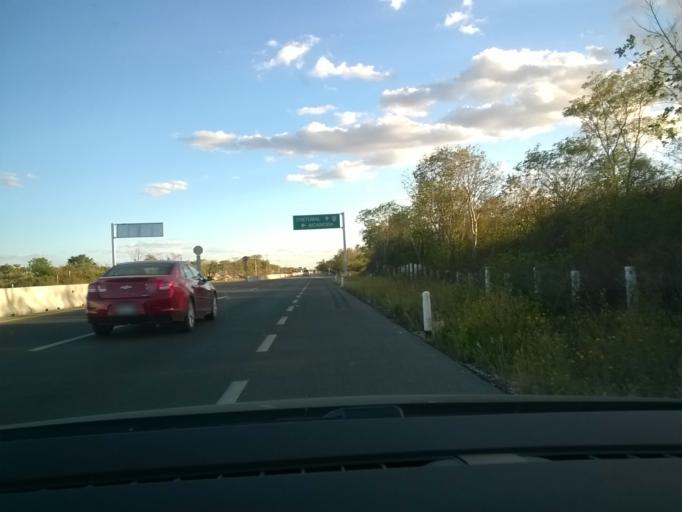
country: MX
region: Yucatan
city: Tekoh
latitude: 20.7483
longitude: -89.4638
